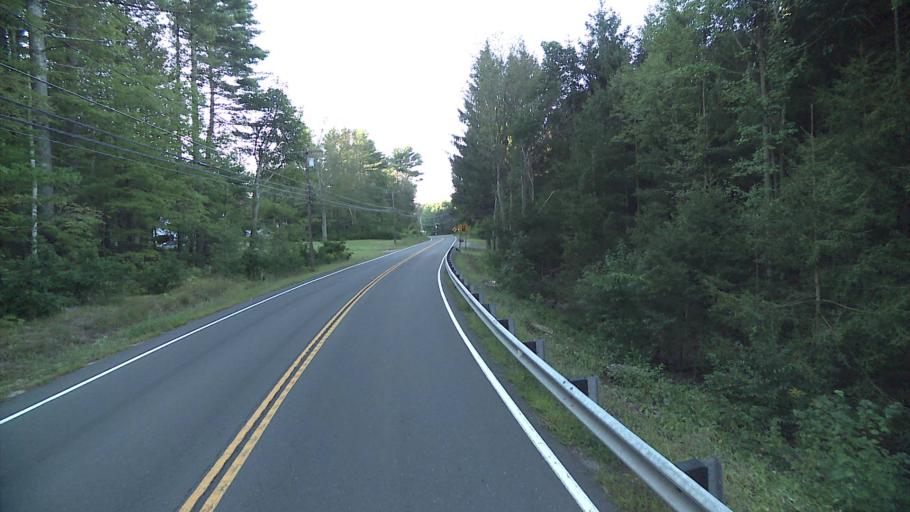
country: US
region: Connecticut
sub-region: Tolland County
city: Stafford
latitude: 41.9783
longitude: -72.3143
